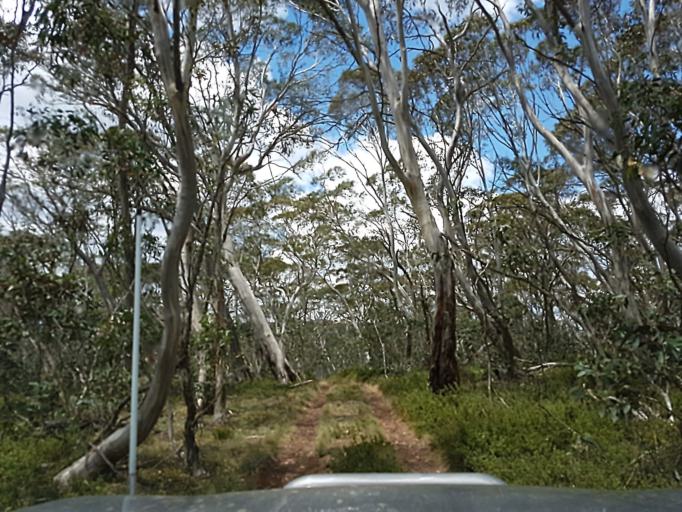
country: AU
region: New South Wales
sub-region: Snowy River
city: Jindabyne
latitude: -36.9023
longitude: 148.1232
